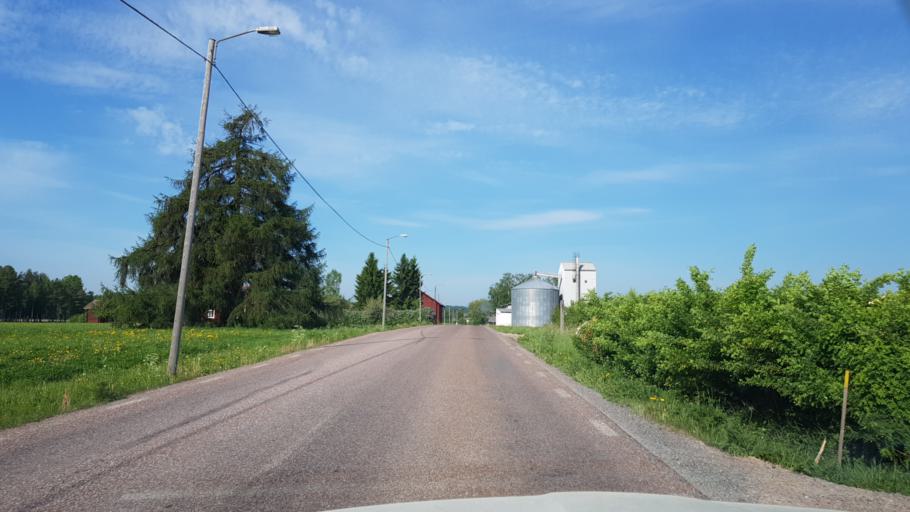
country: SE
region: Dalarna
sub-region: Saters Kommun
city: Saeter
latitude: 60.4173
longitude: 15.7455
